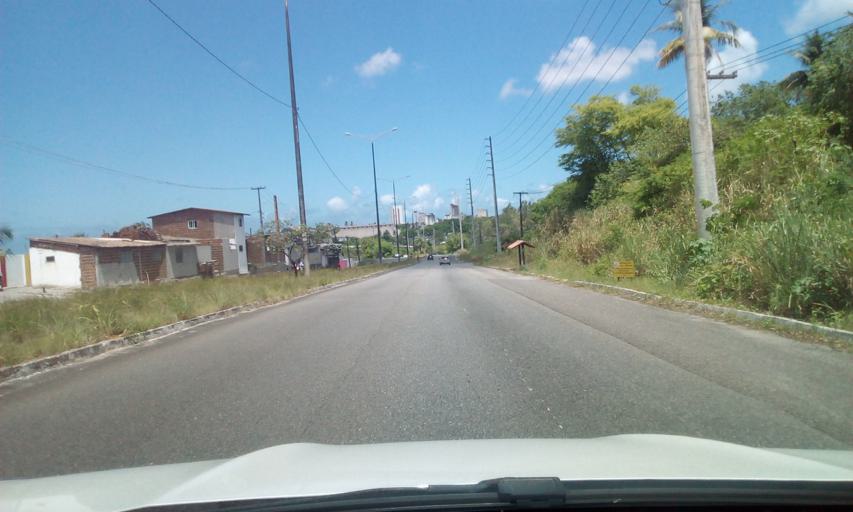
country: BR
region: Paraiba
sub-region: Bayeux
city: Bayeux
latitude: -7.1265
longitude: -34.8987
